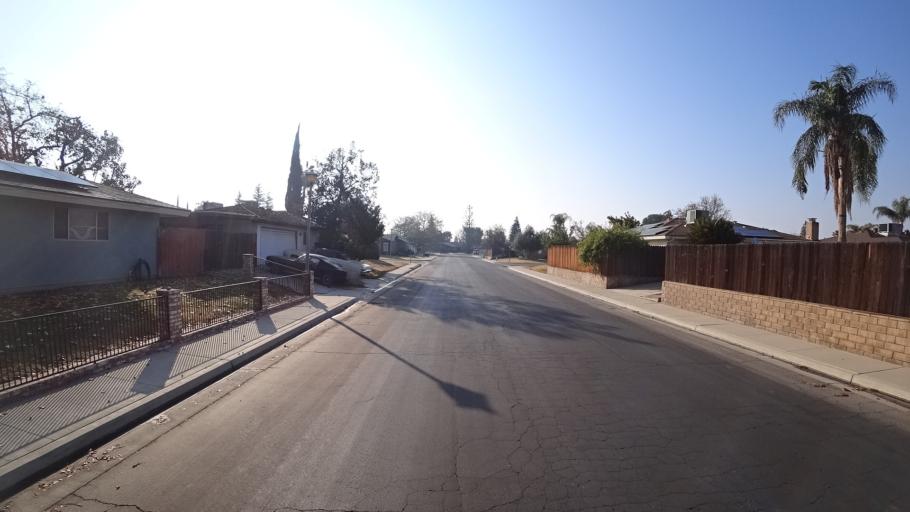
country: US
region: California
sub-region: Kern County
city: Greenacres
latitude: 35.3381
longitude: -119.0756
